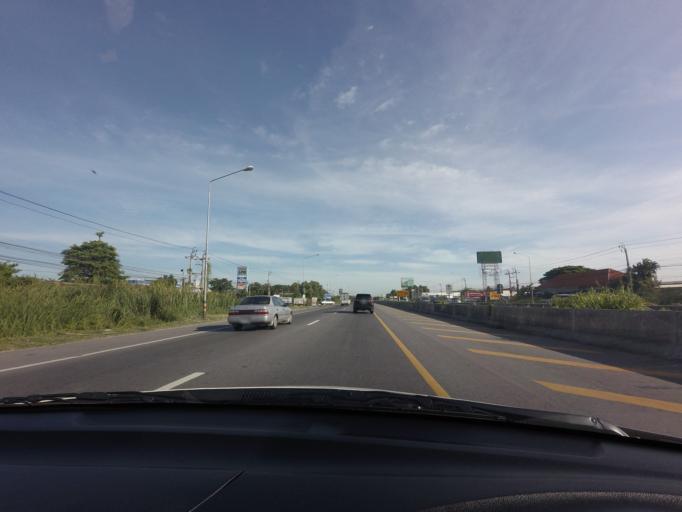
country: TH
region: Nonthaburi
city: Bang Bua Thong
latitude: 13.9478
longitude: 100.4123
